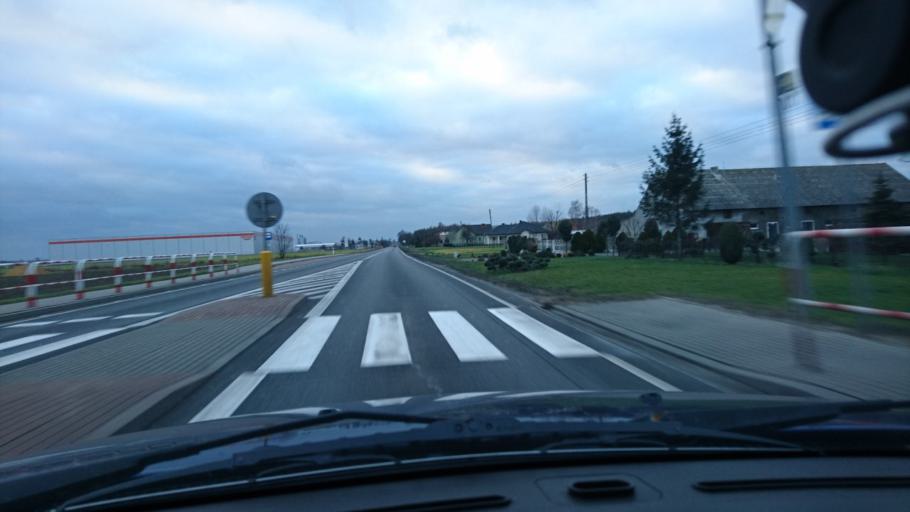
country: PL
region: Greater Poland Voivodeship
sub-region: Powiat kepinski
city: Leka Opatowska
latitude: 51.2245
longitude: 18.1077
